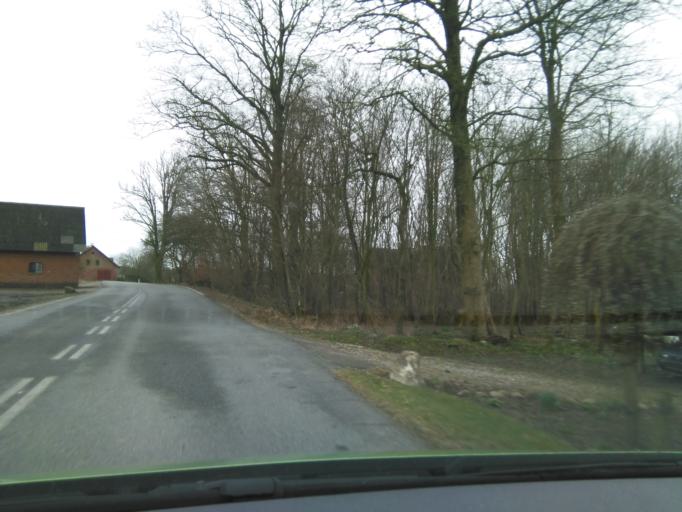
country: DK
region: Central Jutland
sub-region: Odder Kommune
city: Odder
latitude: 55.9956
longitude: 10.1174
